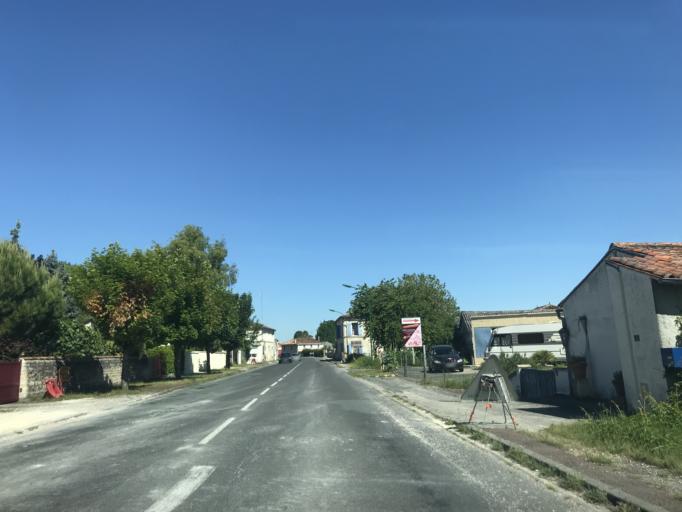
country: FR
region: Poitou-Charentes
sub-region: Departement de la Charente
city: Segonzac
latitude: 45.5240
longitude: -0.2965
